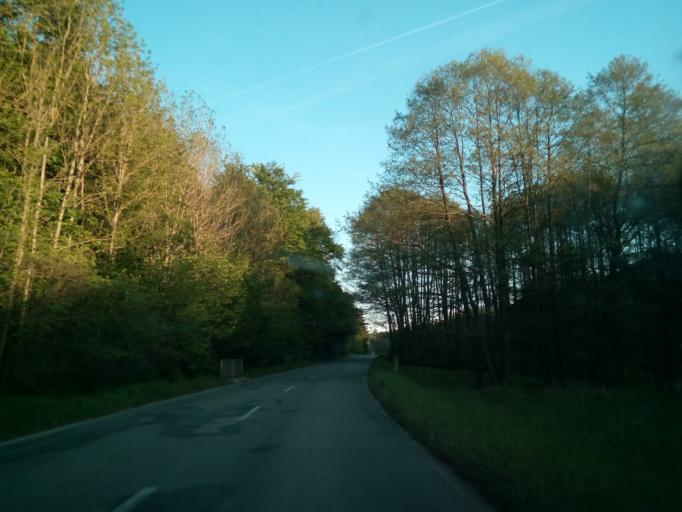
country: CZ
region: South Moravian
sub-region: Okres Blansko
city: Jedovnice
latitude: 49.3171
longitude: 16.7453
